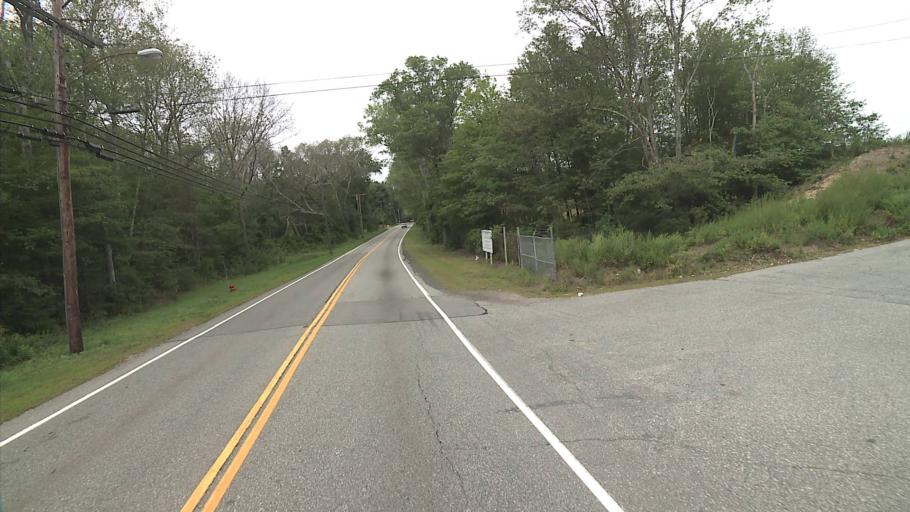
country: US
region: Connecticut
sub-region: New London County
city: Oxoboxo River
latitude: 41.4049
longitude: -72.1816
